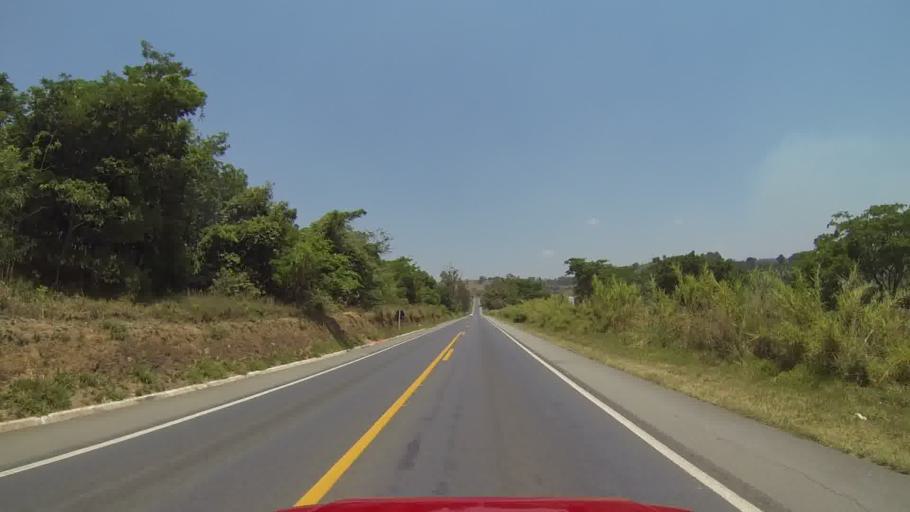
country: BR
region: Minas Gerais
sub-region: Itapecerica
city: Itapecerica
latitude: -20.3322
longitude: -45.2301
